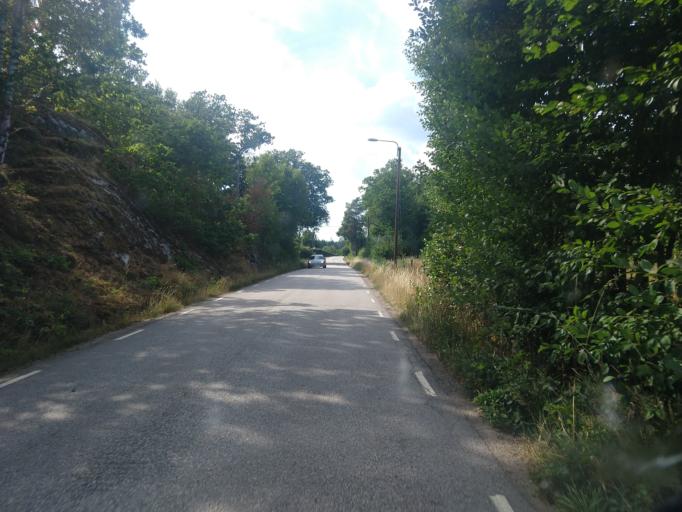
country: SE
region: Blekinge
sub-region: Karlskrona Kommun
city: Rodeby
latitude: 56.2293
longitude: 15.5832
